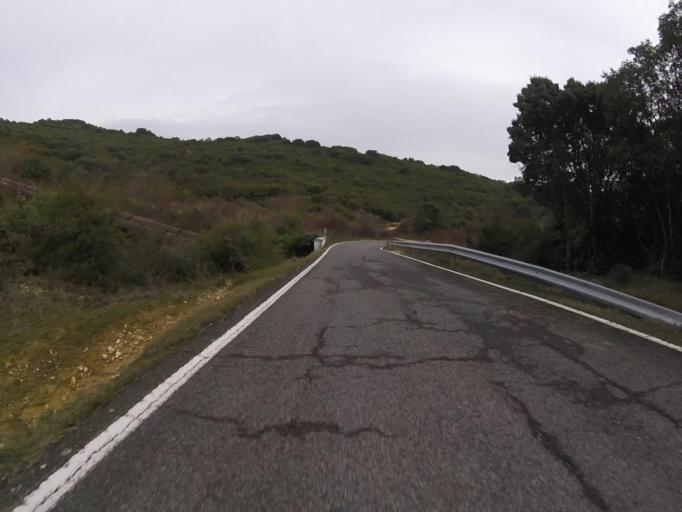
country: ES
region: Navarre
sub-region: Provincia de Navarra
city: Estella
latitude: 42.6983
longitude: -2.0521
